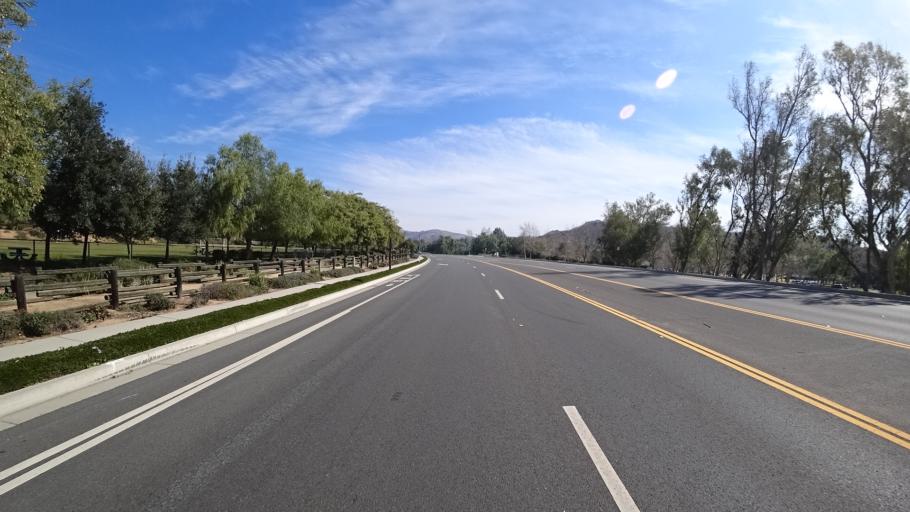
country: US
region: California
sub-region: Orange County
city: Yorba Linda
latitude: 33.9228
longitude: -117.8386
